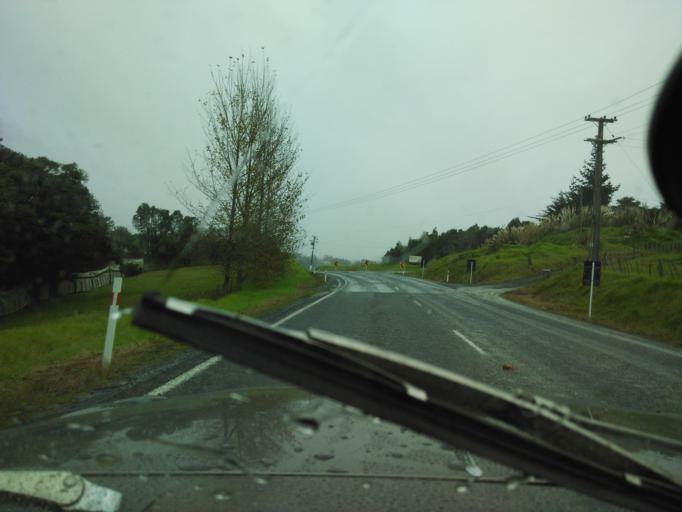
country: NZ
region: Auckland
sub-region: Auckland
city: Wellsford
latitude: -36.3003
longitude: 174.5031
